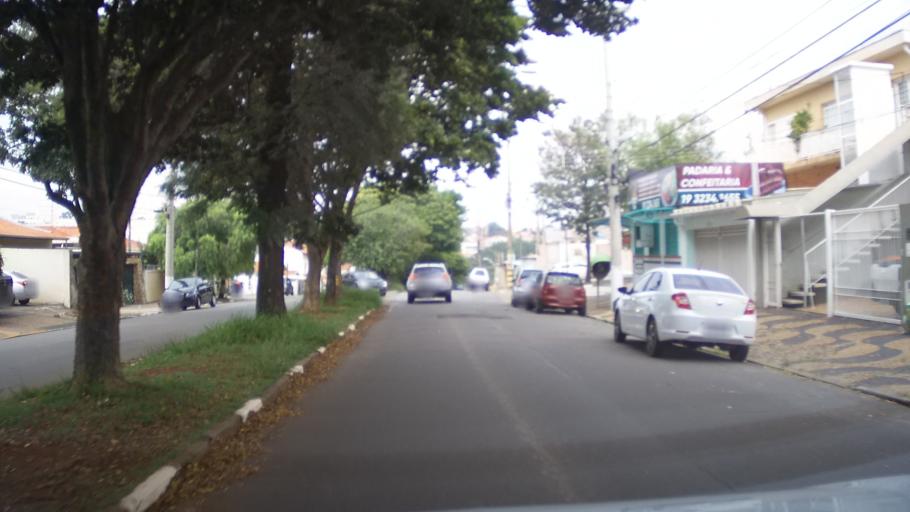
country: BR
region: Sao Paulo
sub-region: Campinas
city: Campinas
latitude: -22.9261
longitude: -47.0576
